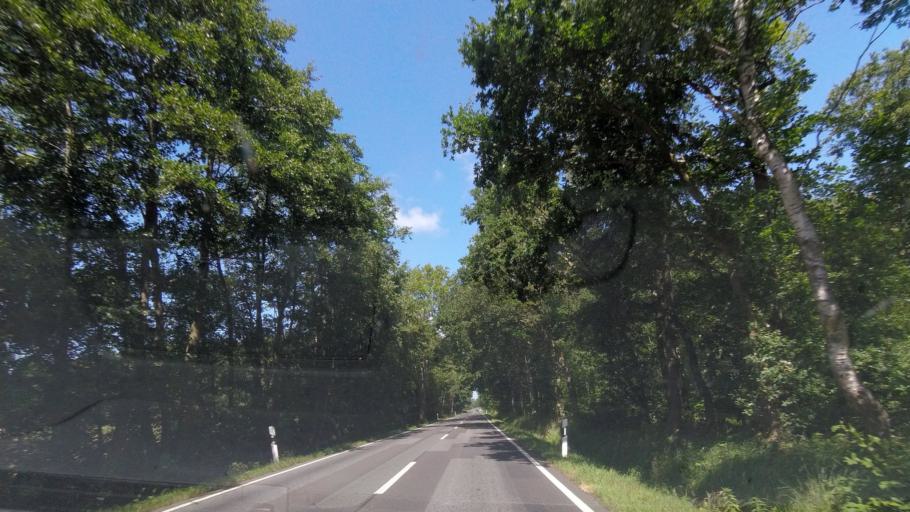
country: DE
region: Mecklenburg-Vorpommern
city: Gingst
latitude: 54.4304
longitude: 13.2743
